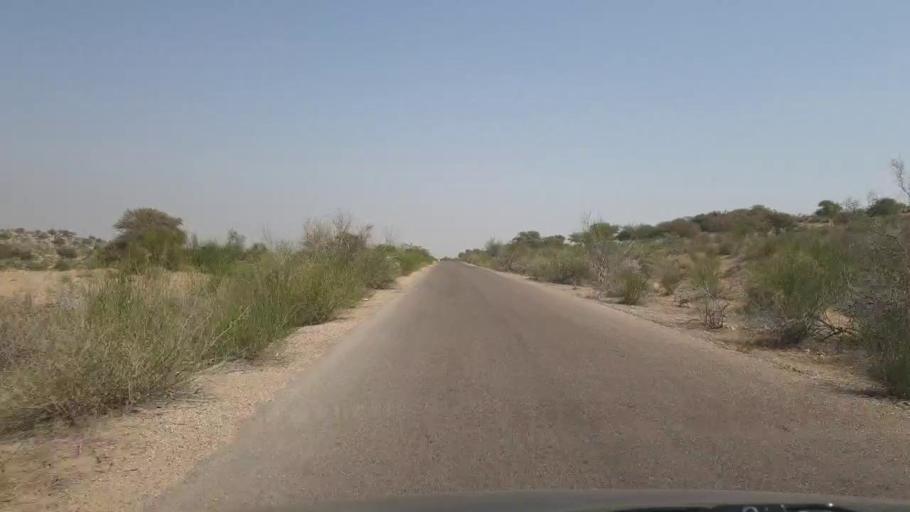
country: PK
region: Sindh
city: Chor
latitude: 25.6609
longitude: 70.1289
